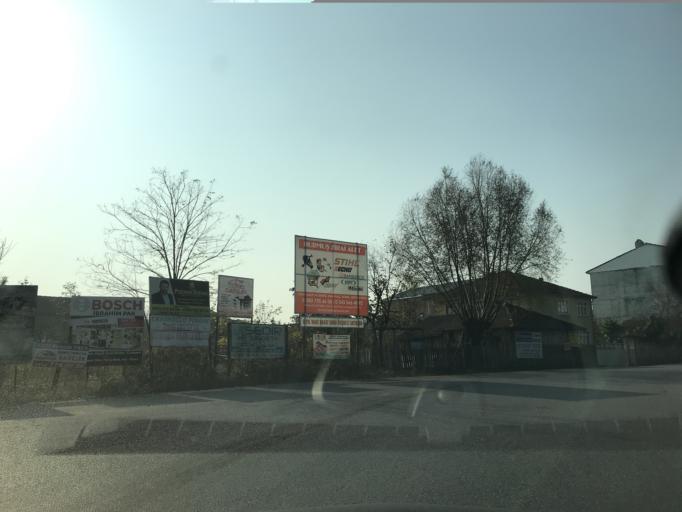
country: TR
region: Duzce
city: Cumayeri
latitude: 40.8844
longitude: 30.9521
